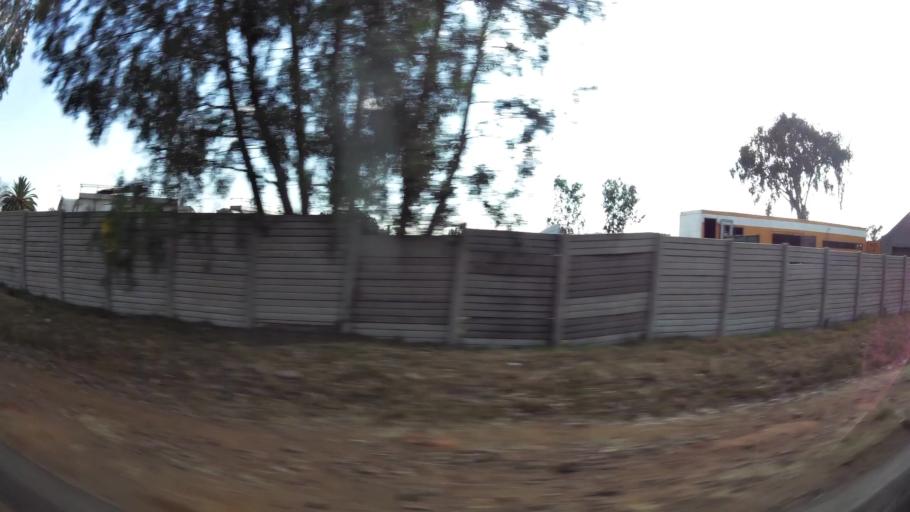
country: ZA
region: Gauteng
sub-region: Ekurhuleni Metropolitan Municipality
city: Benoni
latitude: -26.1016
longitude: 28.3541
